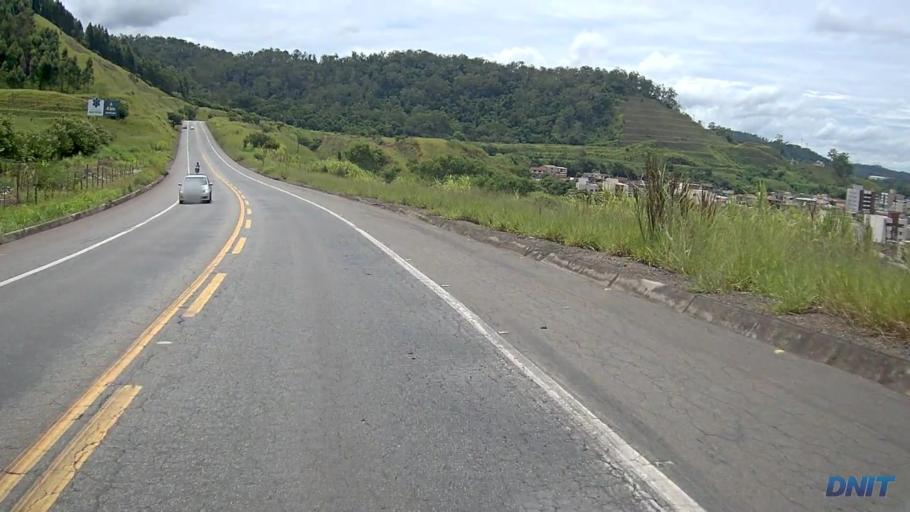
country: BR
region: Minas Gerais
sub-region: Coronel Fabriciano
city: Coronel Fabriciano
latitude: -19.5300
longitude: -42.6317
